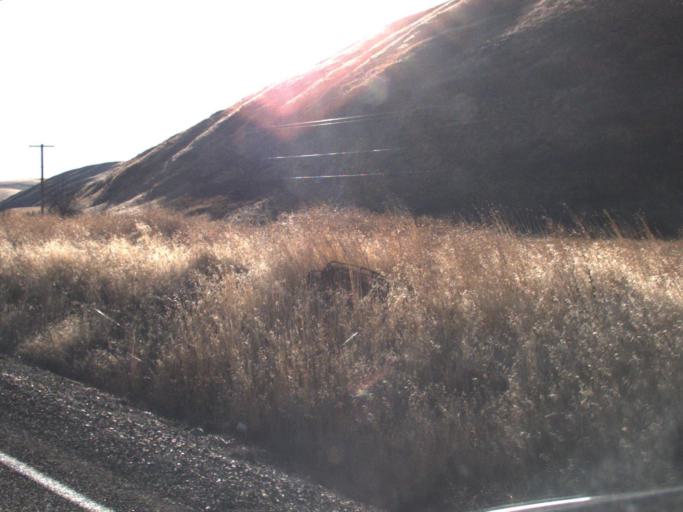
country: US
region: Washington
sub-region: Garfield County
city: Pomeroy
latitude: 46.4849
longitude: -117.7470
